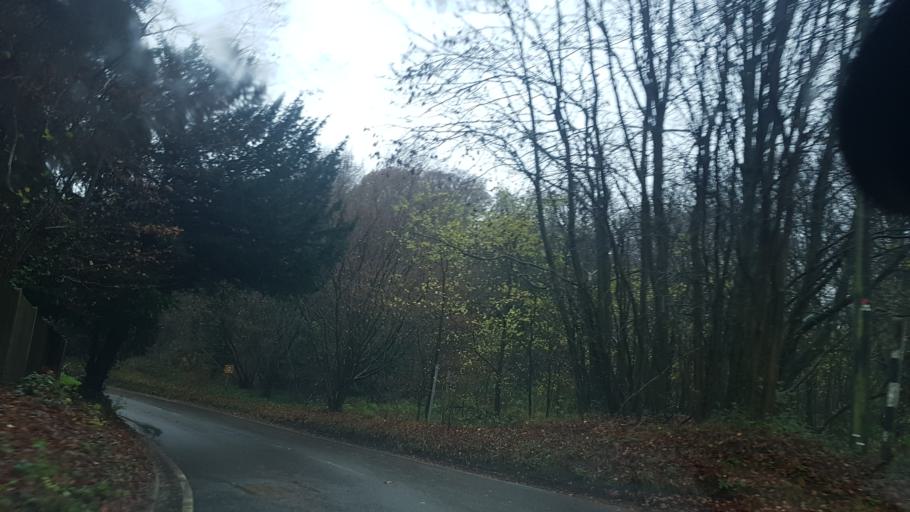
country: GB
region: England
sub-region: Surrey
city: Headley
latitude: 51.2761
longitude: -0.2779
